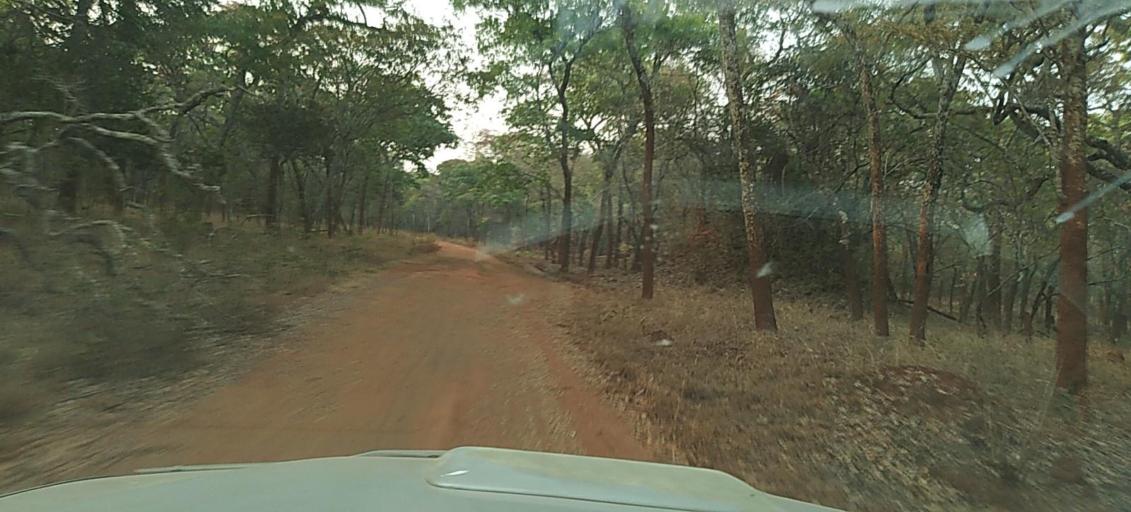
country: ZM
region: North-Western
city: Kasempa
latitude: -13.1059
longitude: 26.4052
